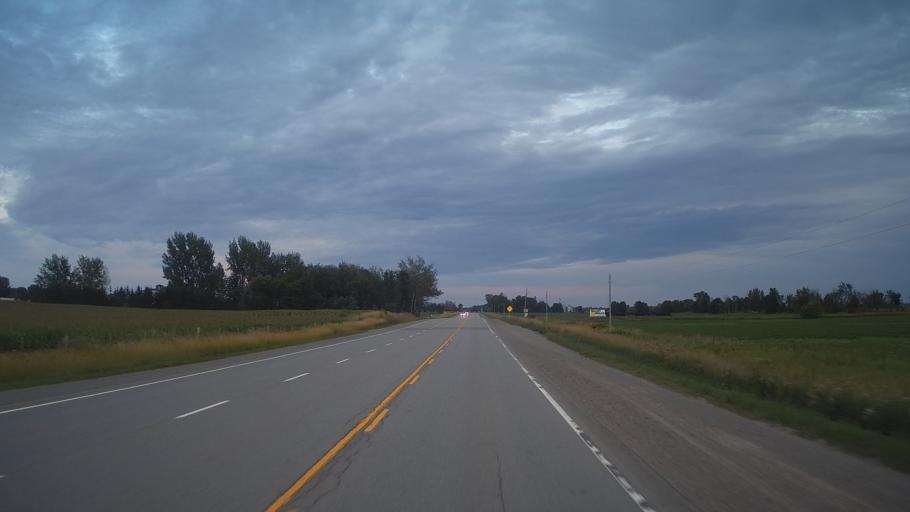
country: CA
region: Ontario
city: Pembroke
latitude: 45.6615
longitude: -76.9187
